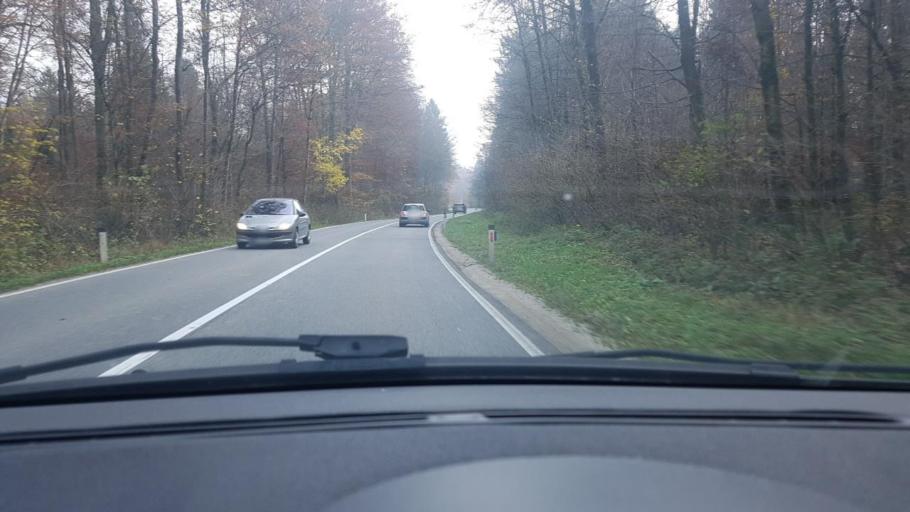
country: SI
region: Vodice
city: Vodice
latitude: 46.2123
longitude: 14.5101
